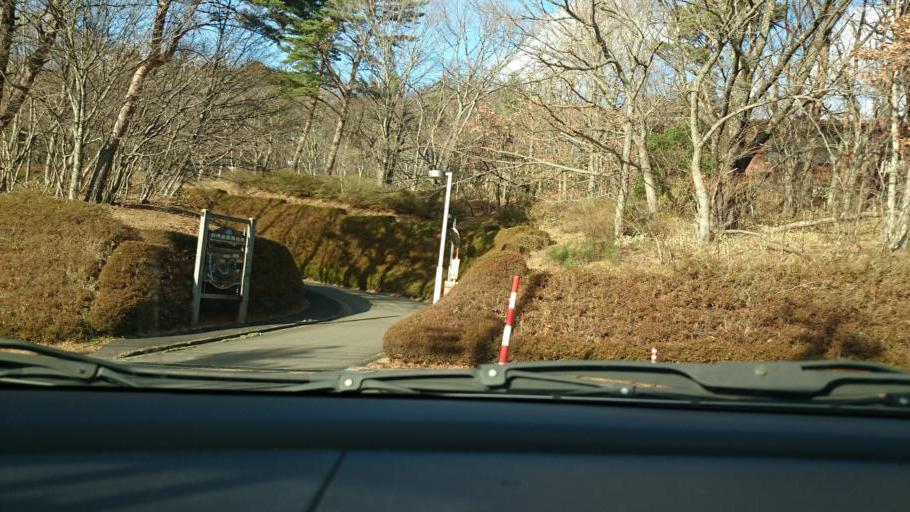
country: JP
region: Tochigi
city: Kuroiso
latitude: 37.1750
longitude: 140.0414
